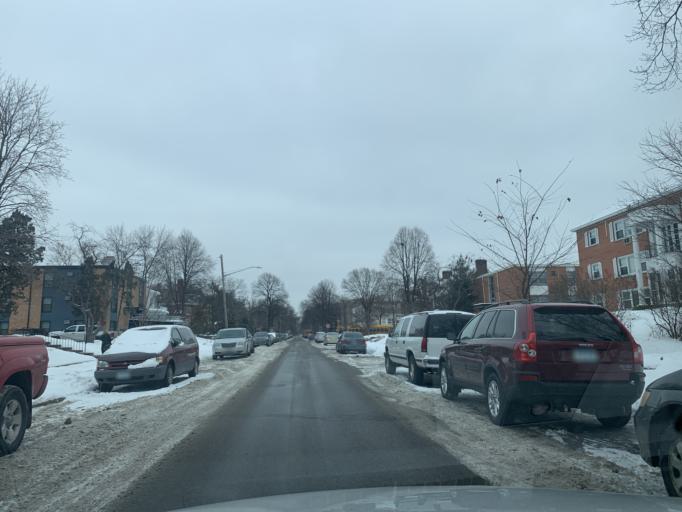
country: US
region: Minnesota
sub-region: Hennepin County
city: Minneapolis
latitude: 44.9563
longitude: -93.2813
